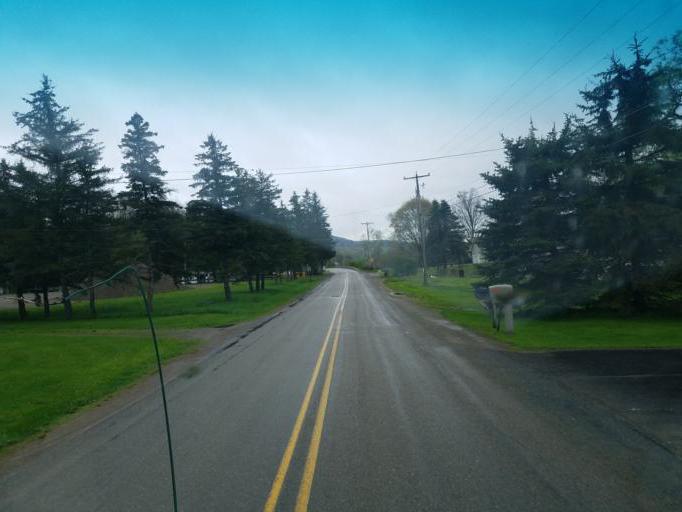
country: US
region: New York
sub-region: Allegany County
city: Wellsville
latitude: 41.9850
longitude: -77.8608
